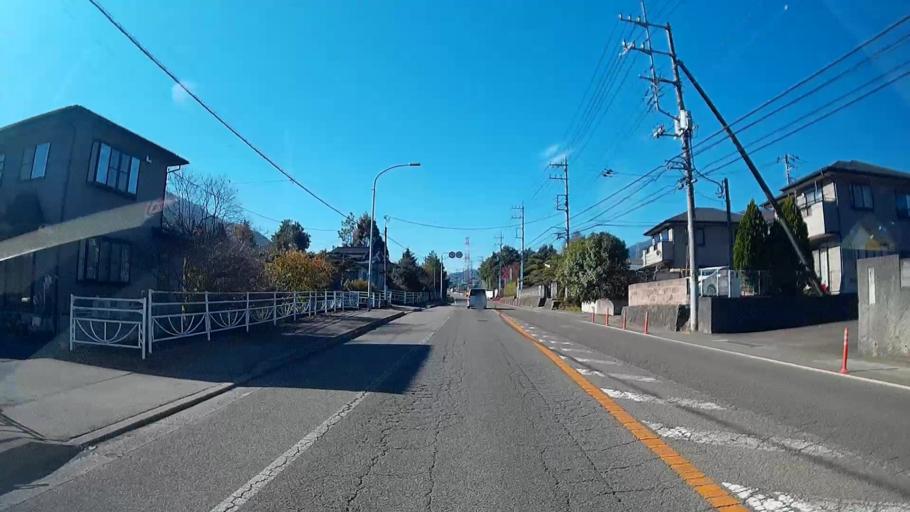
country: JP
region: Yamanashi
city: Otsuki
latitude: 35.5340
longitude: 138.8680
